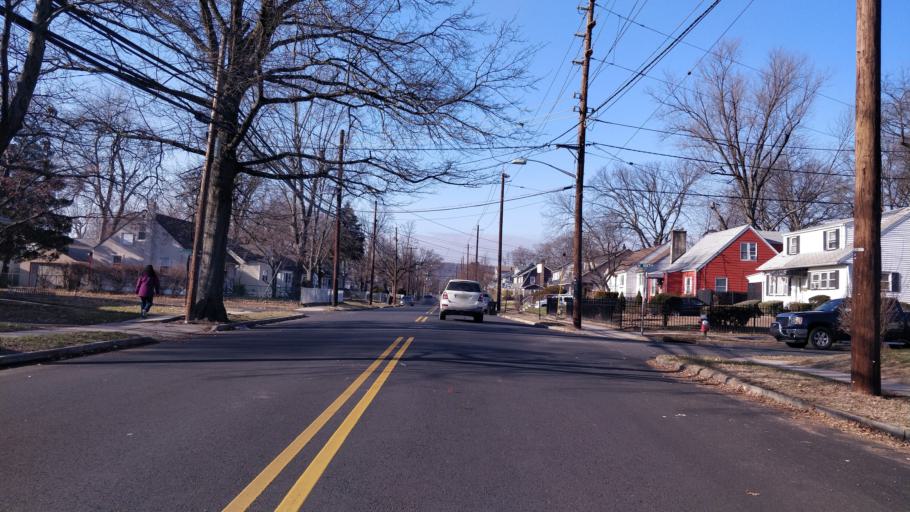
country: US
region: New Jersey
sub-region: Middlesex County
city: South Plainfield
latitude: 40.5978
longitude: -74.4387
